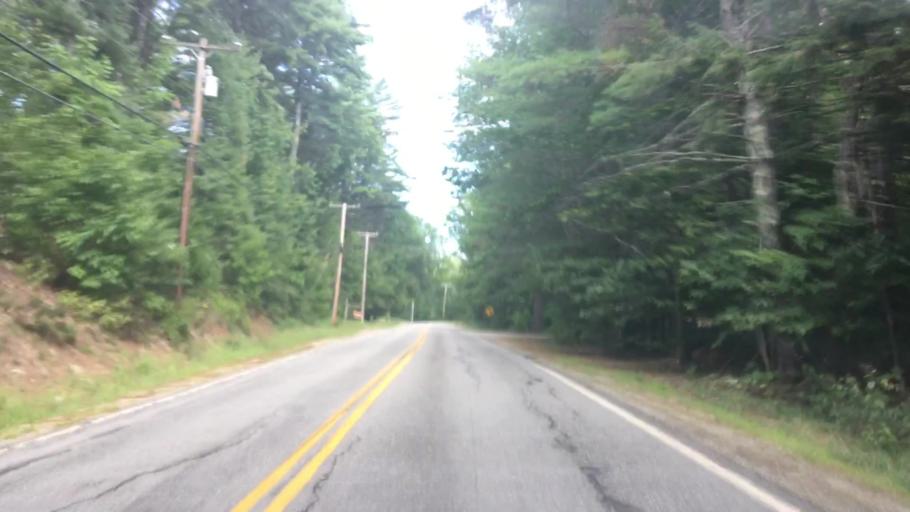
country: US
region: Maine
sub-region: Oxford County
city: Oxford
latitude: 44.0965
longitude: -70.5142
